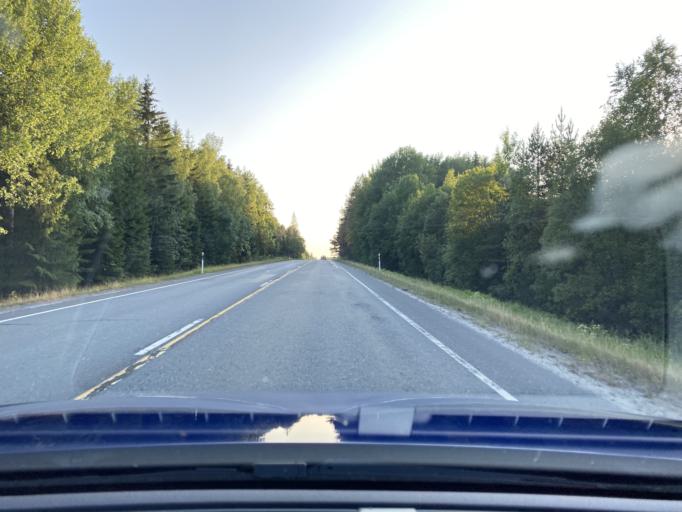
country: FI
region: Haeme
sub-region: Forssa
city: Tammela
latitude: 60.8304
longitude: 23.7037
